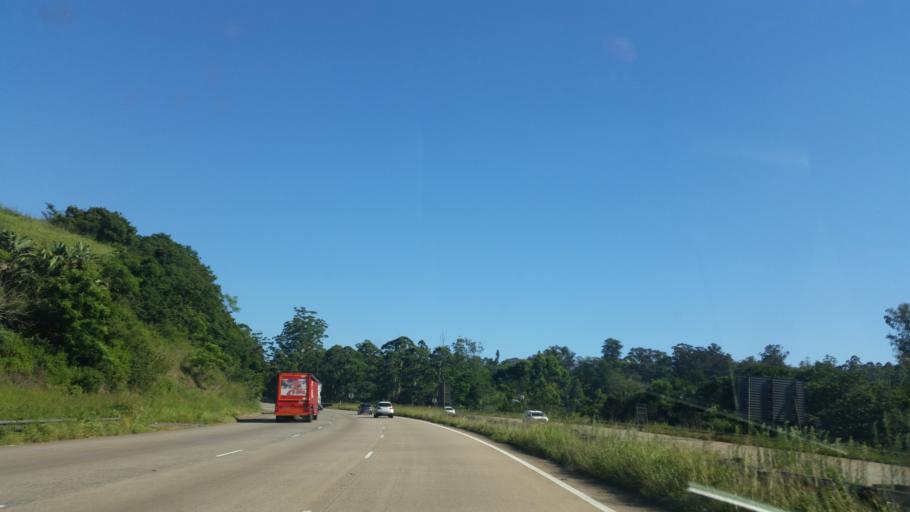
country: ZA
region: KwaZulu-Natal
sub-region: eThekwini Metropolitan Municipality
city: Mpumalanga
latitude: -29.7450
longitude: 30.6632
